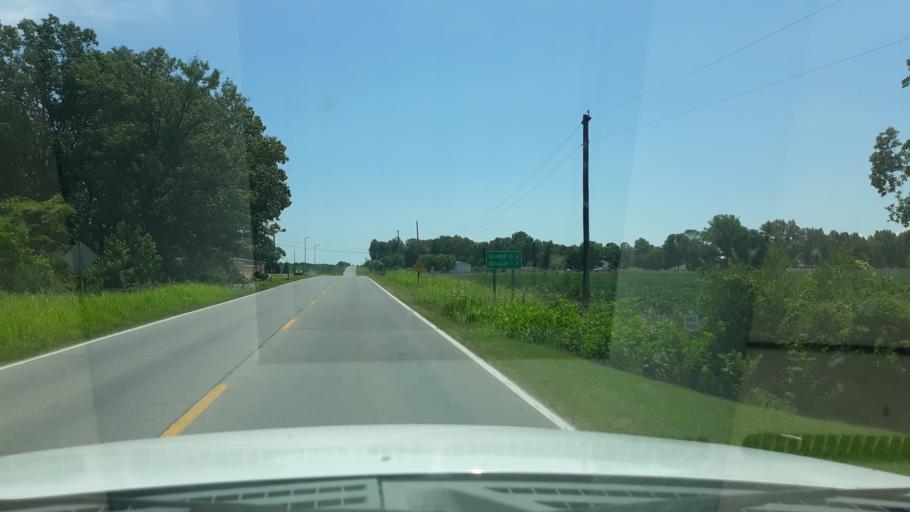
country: US
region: Illinois
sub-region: Saline County
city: Eldorado
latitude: 37.8039
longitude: -88.4339
